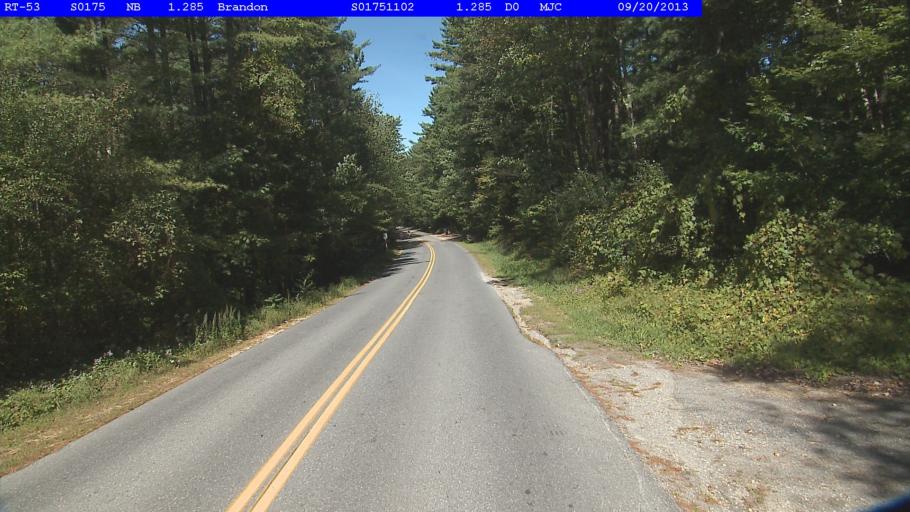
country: US
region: Vermont
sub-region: Rutland County
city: Brandon
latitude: 43.8453
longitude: -73.0571
